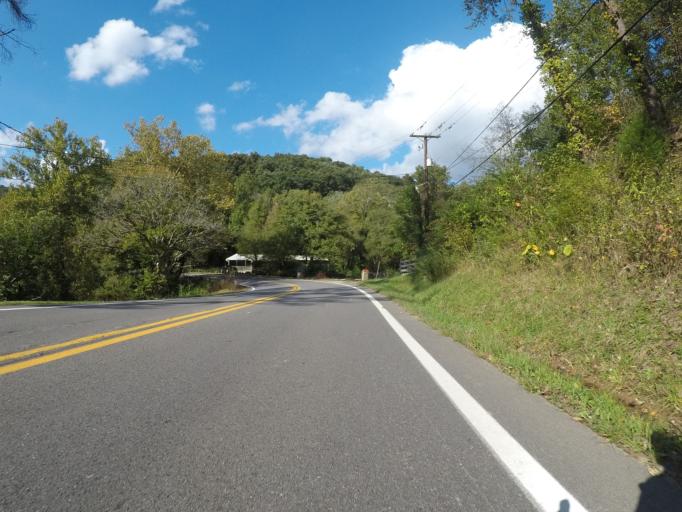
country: US
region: Ohio
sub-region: Lawrence County
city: Burlington
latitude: 38.3606
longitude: -82.5054
